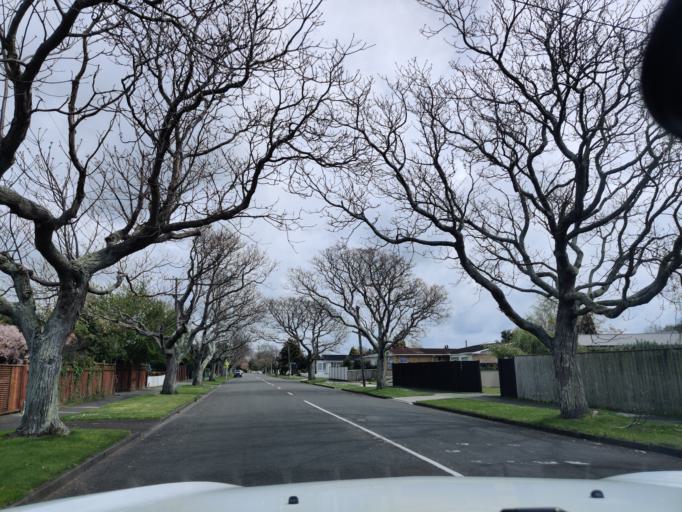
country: NZ
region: Manawatu-Wanganui
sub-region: Palmerston North City
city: Palmerston North
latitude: -40.3778
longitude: 175.5966
